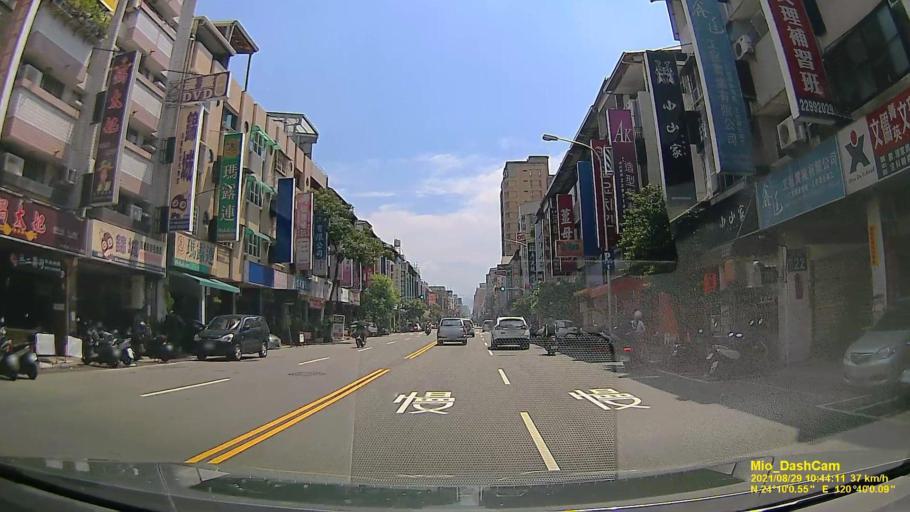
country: TW
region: Taiwan
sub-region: Taichung City
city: Taichung
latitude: 24.1668
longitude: 120.6667
